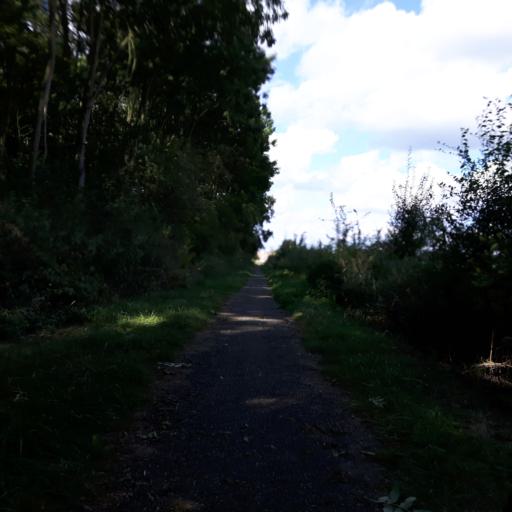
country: NL
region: Zeeland
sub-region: Gemeente Goes
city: Goes
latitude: 51.4888
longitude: 3.8294
